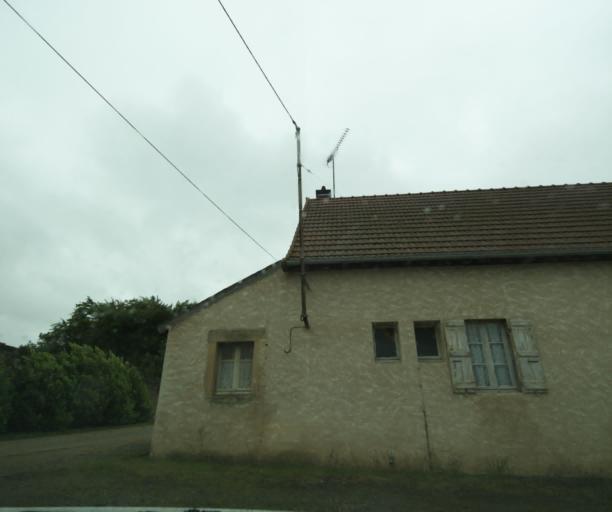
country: FR
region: Bourgogne
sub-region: Departement de Saone-et-Loire
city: Palinges
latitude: 46.5223
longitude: 4.2071
